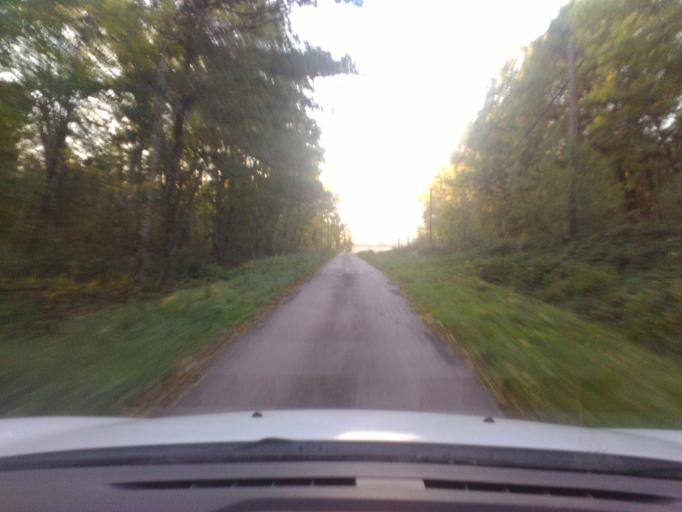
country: FR
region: Lorraine
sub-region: Departement des Vosges
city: Charmes
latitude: 48.3377
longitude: 6.2557
